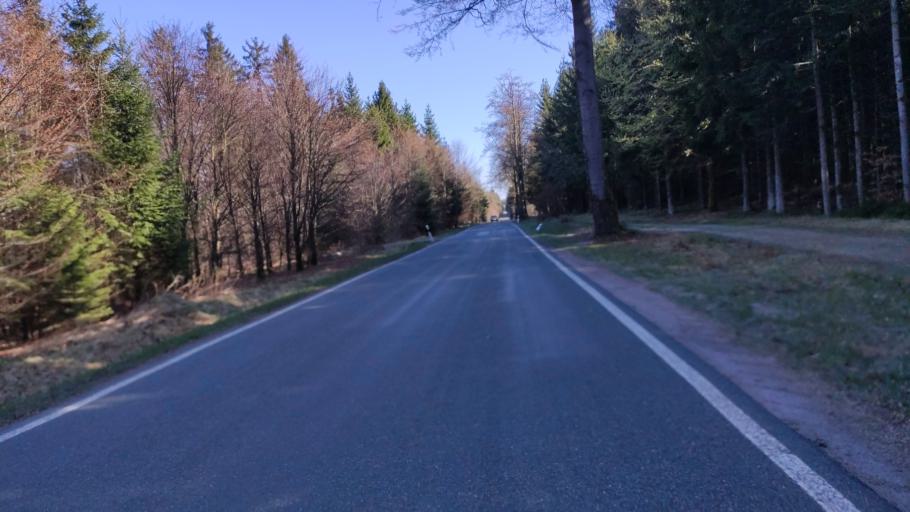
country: DE
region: Bavaria
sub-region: Upper Franconia
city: Tschirn
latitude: 50.4482
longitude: 11.4615
